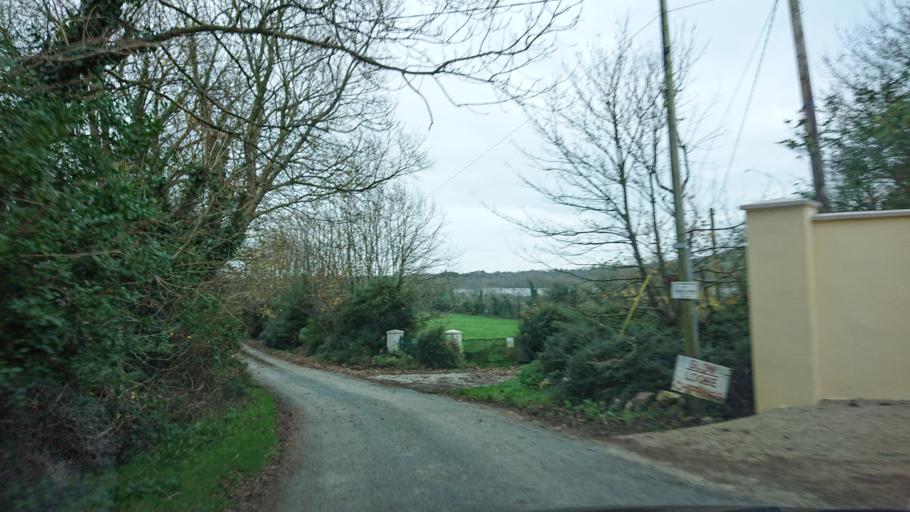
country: IE
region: Munster
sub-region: Waterford
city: Dunmore East
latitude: 52.1912
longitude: -7.0389
